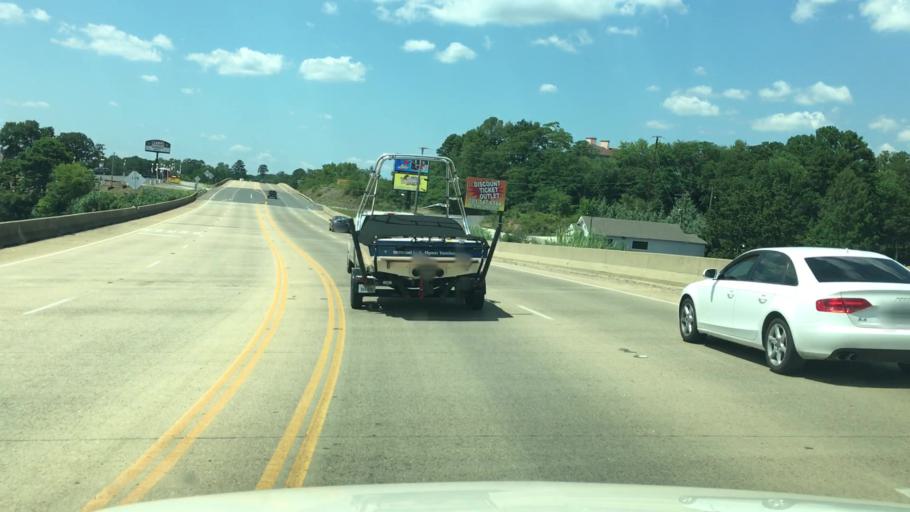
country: US
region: Arkansas
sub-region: Garland County
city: Lake Hamilton
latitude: 34.4297
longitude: -93.0849
